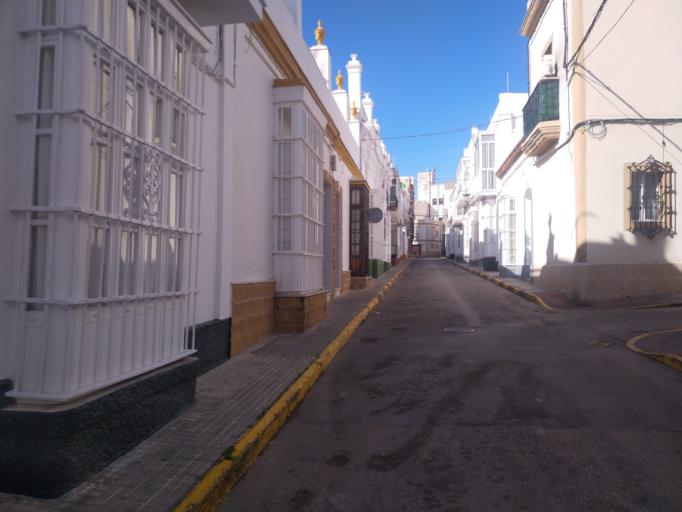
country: ES
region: Andalusia
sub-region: Provincia de Cadiz
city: San Fernando
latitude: 36.4647
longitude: -6.1950
